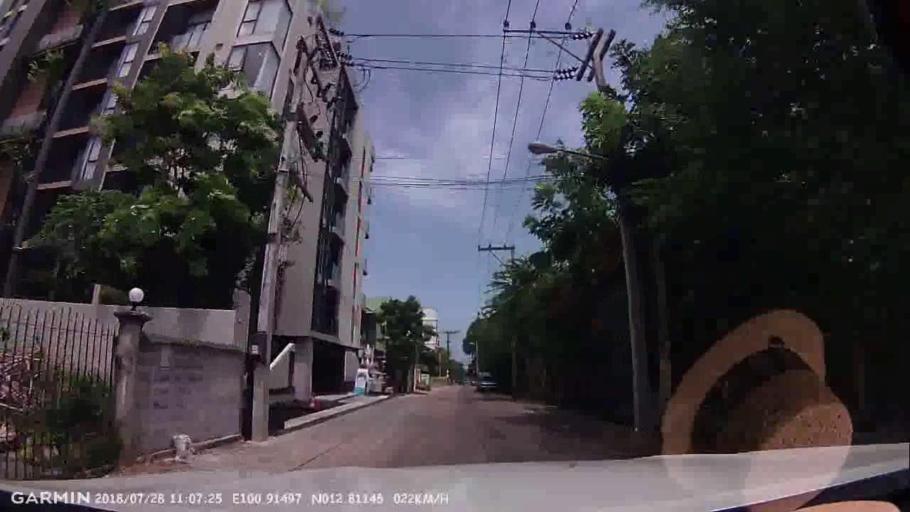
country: TH
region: Chon Buri
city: Phatthaya
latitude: 12.8114
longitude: 100.9149
